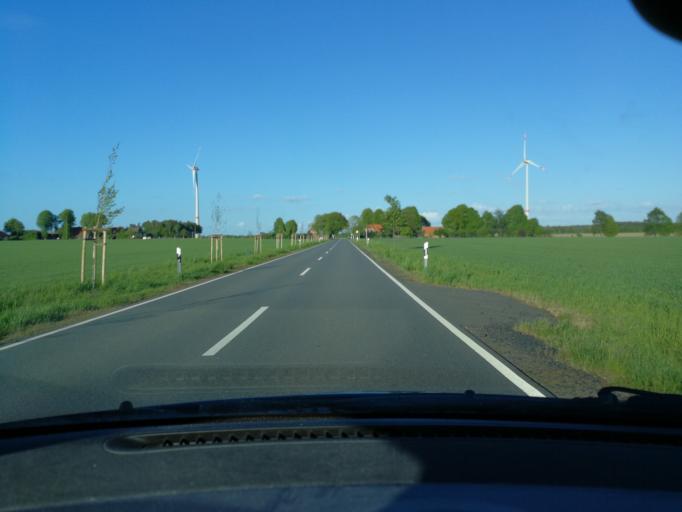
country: DE
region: Lower Saxony
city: Rehlingen
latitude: 53.1019
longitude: 10.2720
